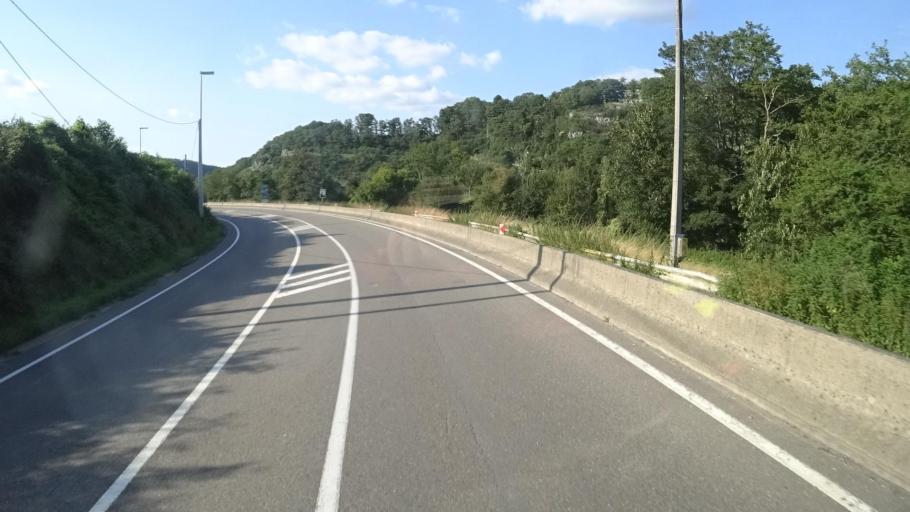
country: BE
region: Wallonia
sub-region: Province de Namur
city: Profondeville
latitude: 50.3547
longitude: 4.8765
